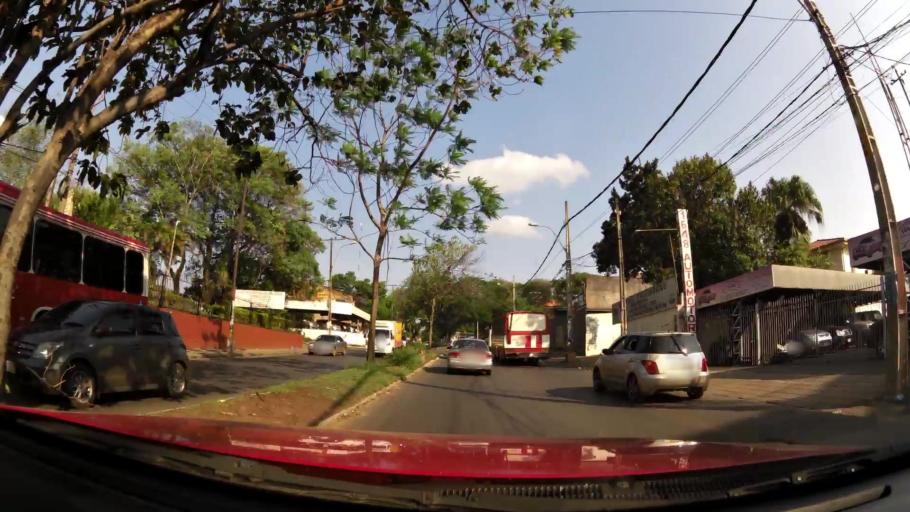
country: PY
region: Central
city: Lambare
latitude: -25.3207
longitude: -57.6048
